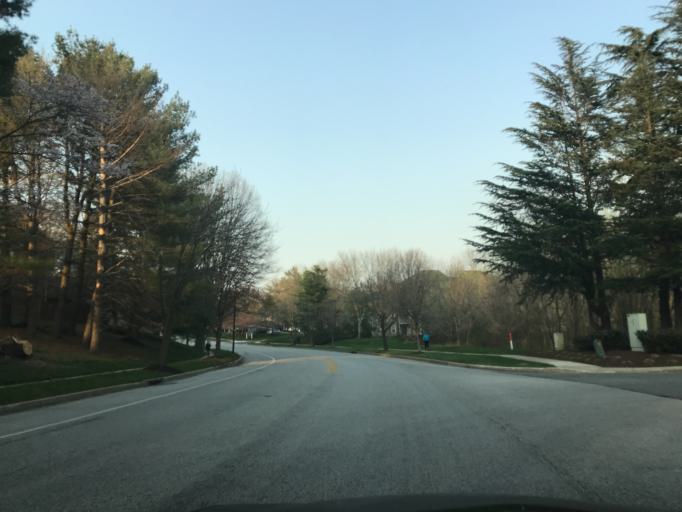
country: US
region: Maryland
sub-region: Howard County
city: Columbia
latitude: 39.2312
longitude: -76.8487
